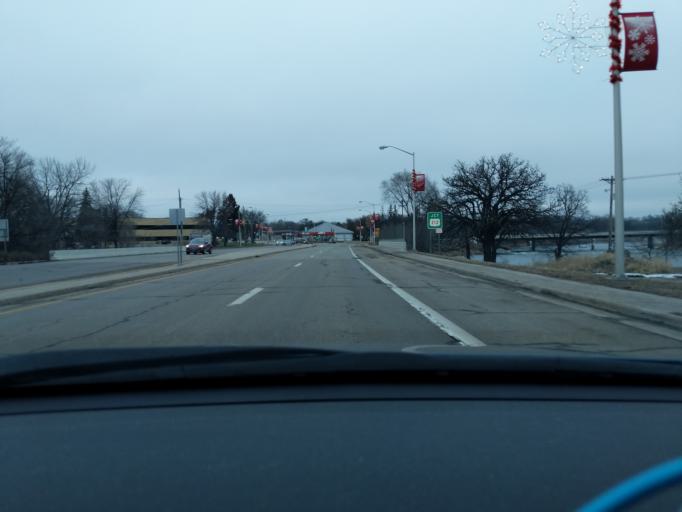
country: US
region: Minnesota
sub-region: Yellow Medicine County
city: Granite Falls
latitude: 44.8034
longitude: -95.5467
